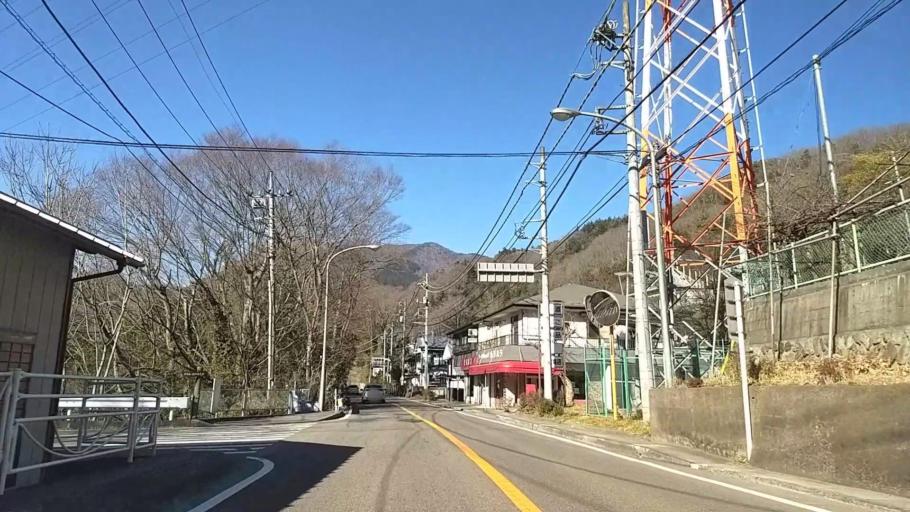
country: JP
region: Yamanashi
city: Uenohara
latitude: 35.6048
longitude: 139.0382
